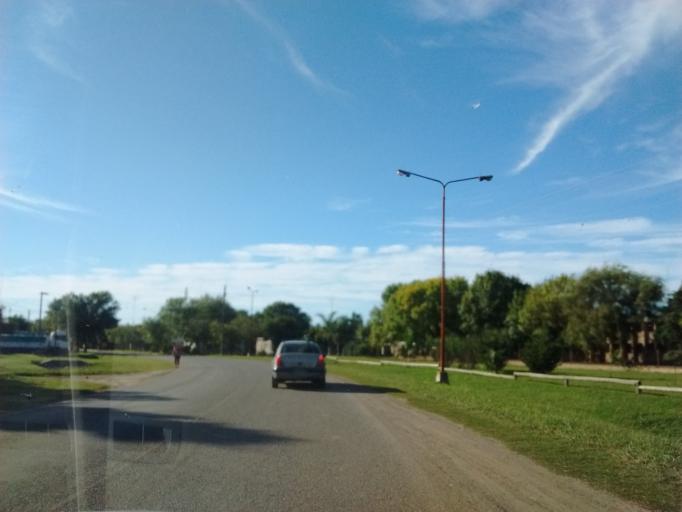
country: AR
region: Santa Fe
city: Coronda
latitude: -32.2308
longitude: -60.9866
